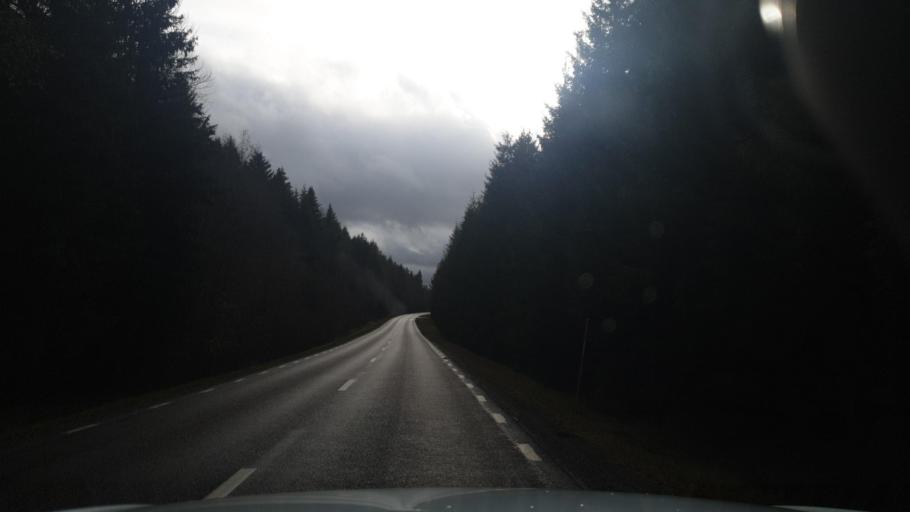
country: SE
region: Vaermland
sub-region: Arjangs Kommun
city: Arjaeng
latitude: 59.6247
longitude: 12.1415
